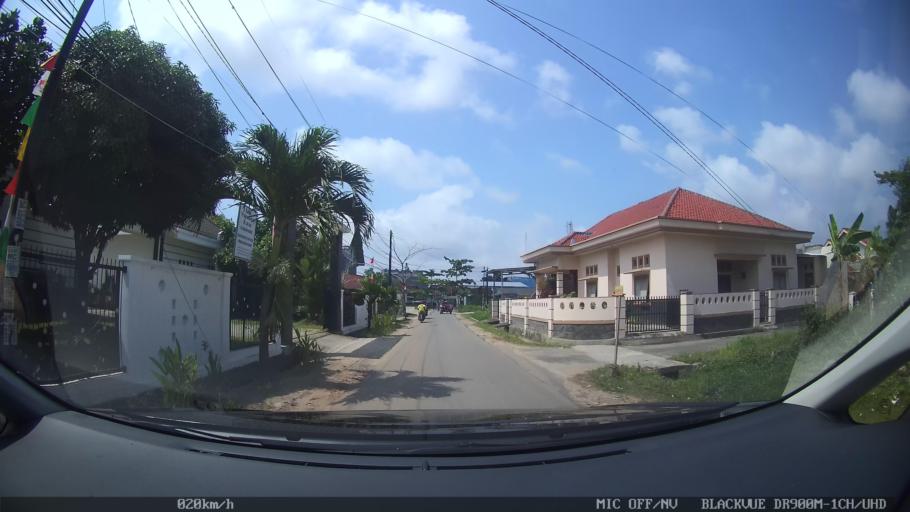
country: ID
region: Lampung
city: Kedaton
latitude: -5.3608
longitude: 105.2794
